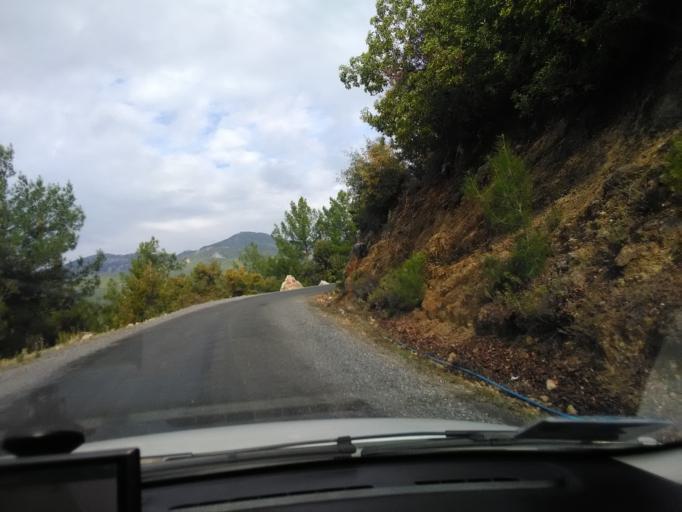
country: TR
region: Antalya
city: Gazipasa
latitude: 36.2467
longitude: 32.4383
